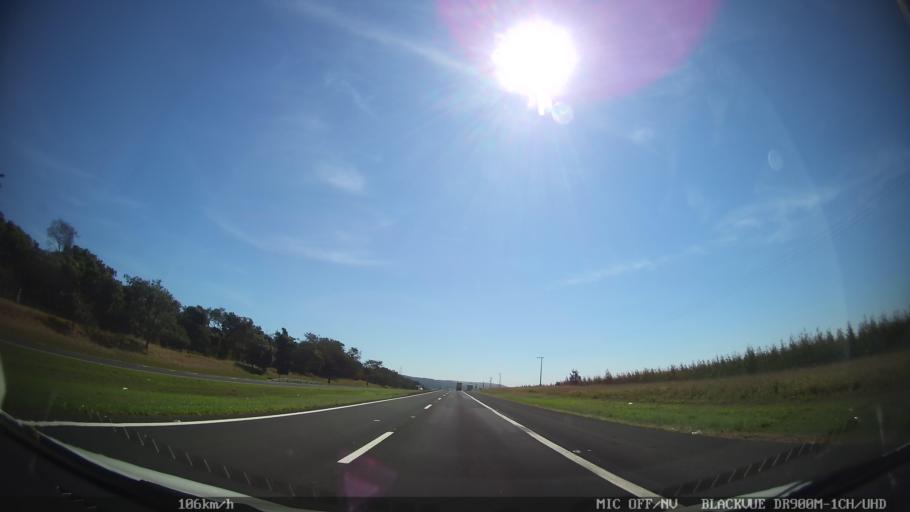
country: BR
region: Sao Paulo
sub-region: Sao Simao
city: Sao Simao
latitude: -21.5371
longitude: -47.6408
